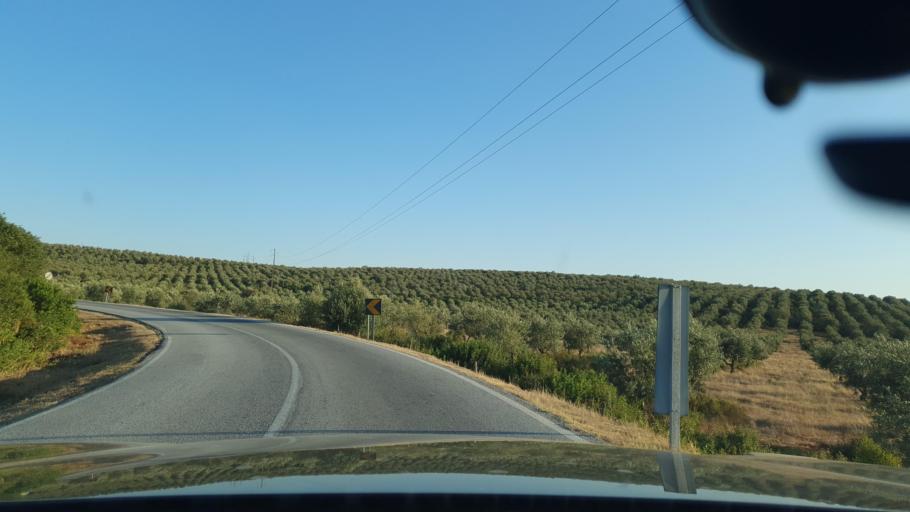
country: PT
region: Evora
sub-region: Estremoz
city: Estremoz
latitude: 38.9216
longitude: -7.6678
